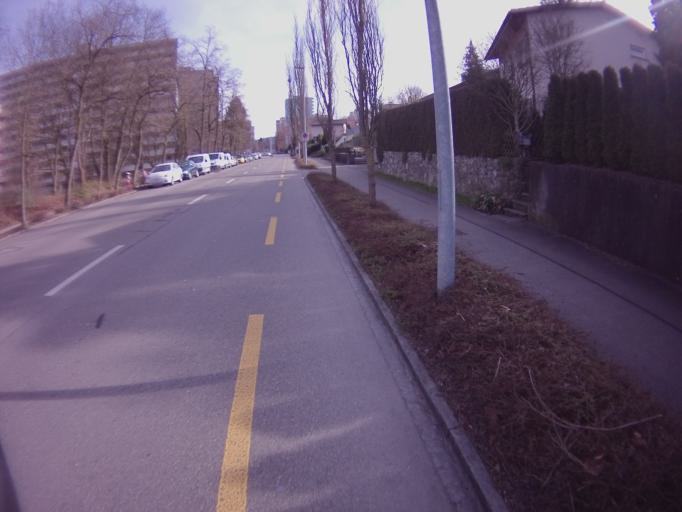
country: CH
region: Aargau
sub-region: Bezirk Baden
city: Spreitenbach
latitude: 47.4274
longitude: 8.3596
